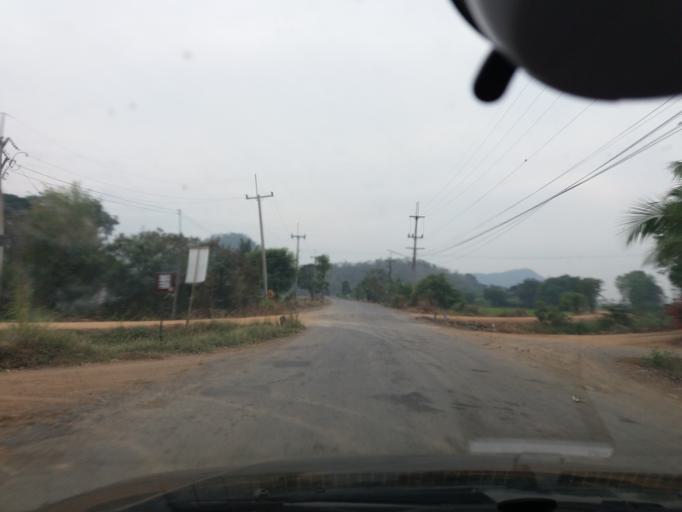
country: TH
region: Suphan Buri
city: Doembang Nangbuat
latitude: 14.8366
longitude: 100.1227
